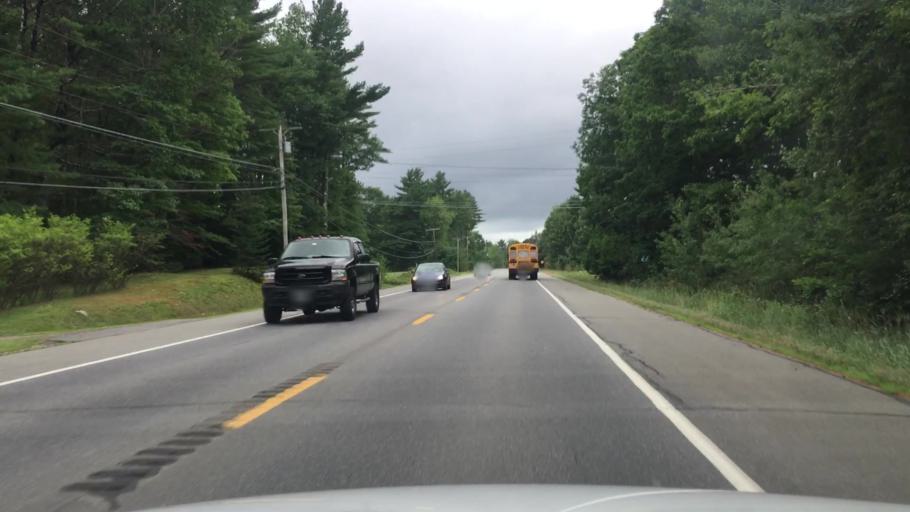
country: US
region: Maine
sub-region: Kennebec County
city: Windsor
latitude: 44.2693
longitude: -69.5758
